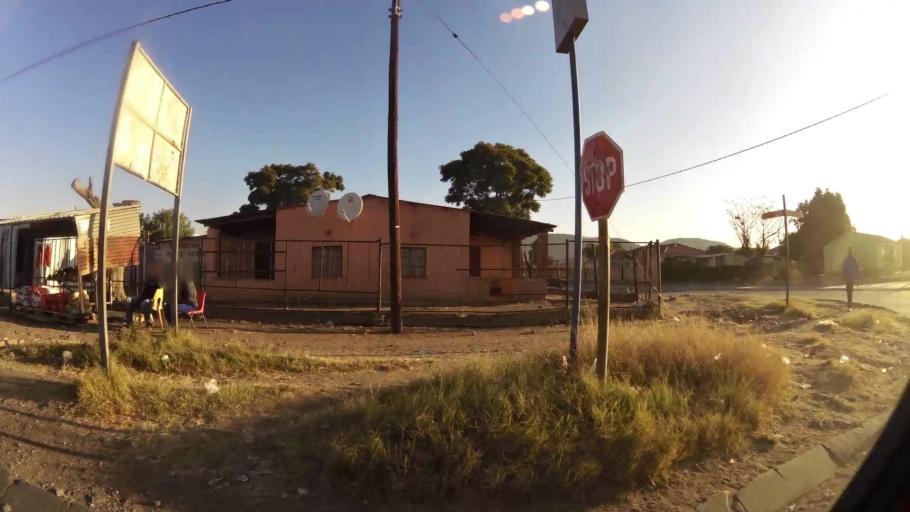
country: ZA
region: North-West
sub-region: Bojanala Platinum District Municipality
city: Rustenburg
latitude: -25.6356
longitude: 27.2197
